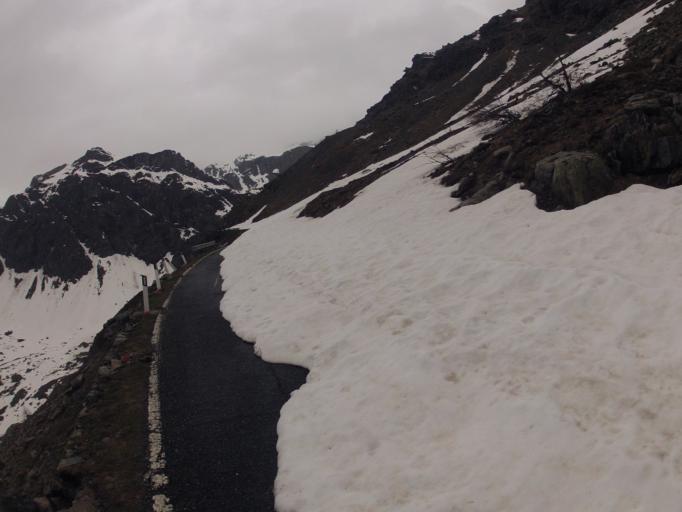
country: IT
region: Piedmont
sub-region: Provincia di Cuneo
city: Crissolo
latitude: 44.7022
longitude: 7.1064
